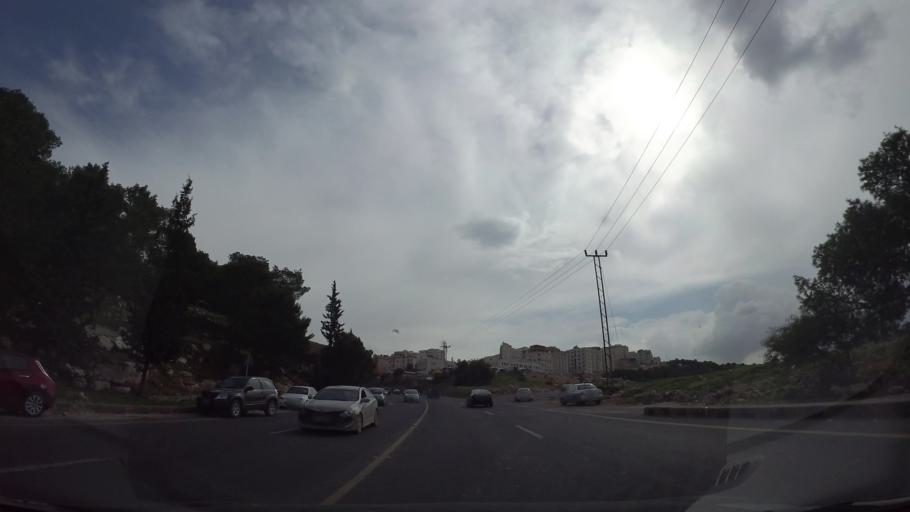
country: JO
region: Amman
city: Amman
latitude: 32.0112
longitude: 35.9334
